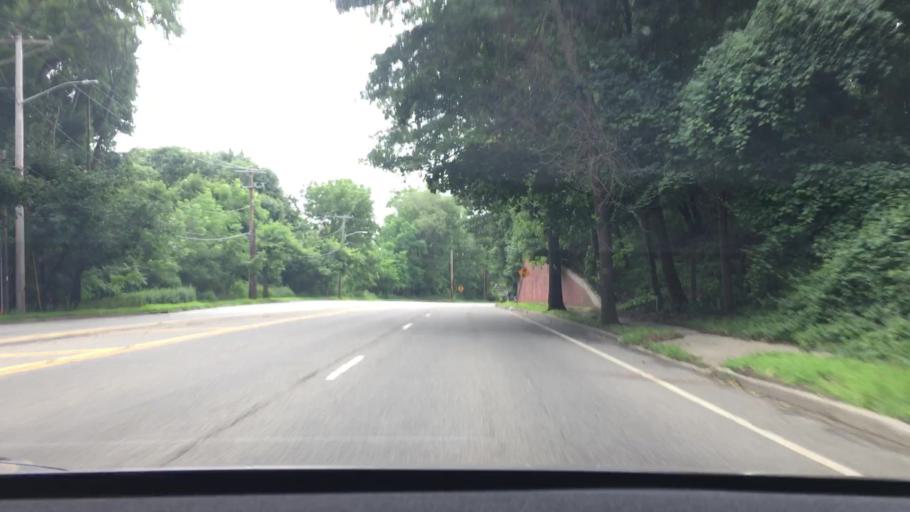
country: US
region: New York
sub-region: Nassau County
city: Woodbury
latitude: 40.8115
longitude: -73.4695
